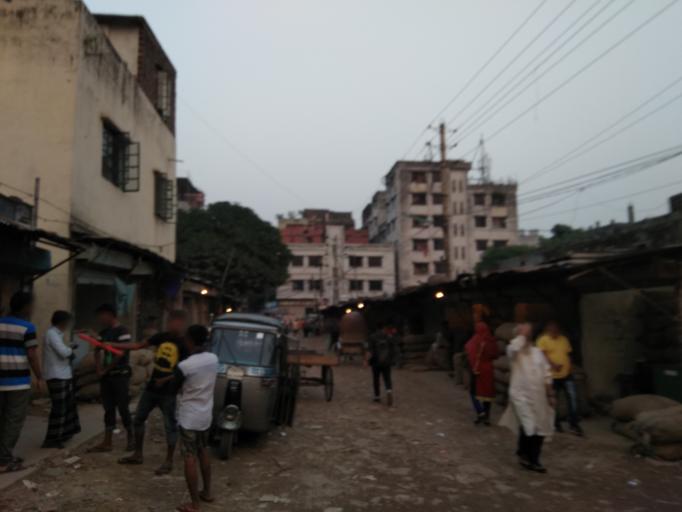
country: BD
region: Dhaka
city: Tungi
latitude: 23.8149
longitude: 90.3691
